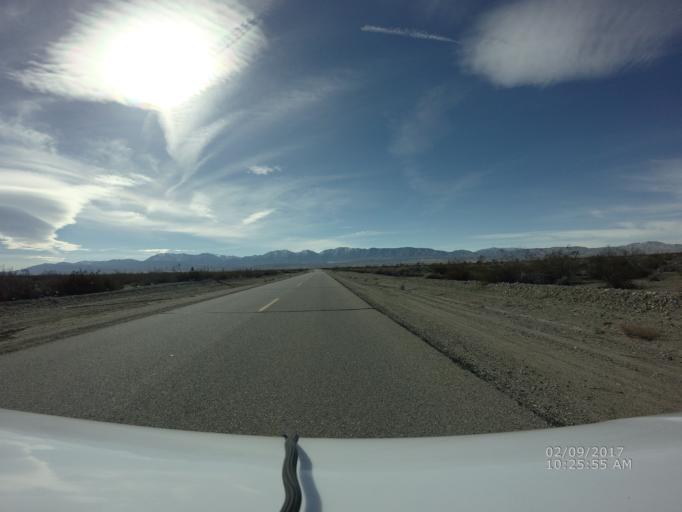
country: US
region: California
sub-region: Los Angeles County
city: Lake Los Angeles
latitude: 34.5523
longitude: -117.8901
